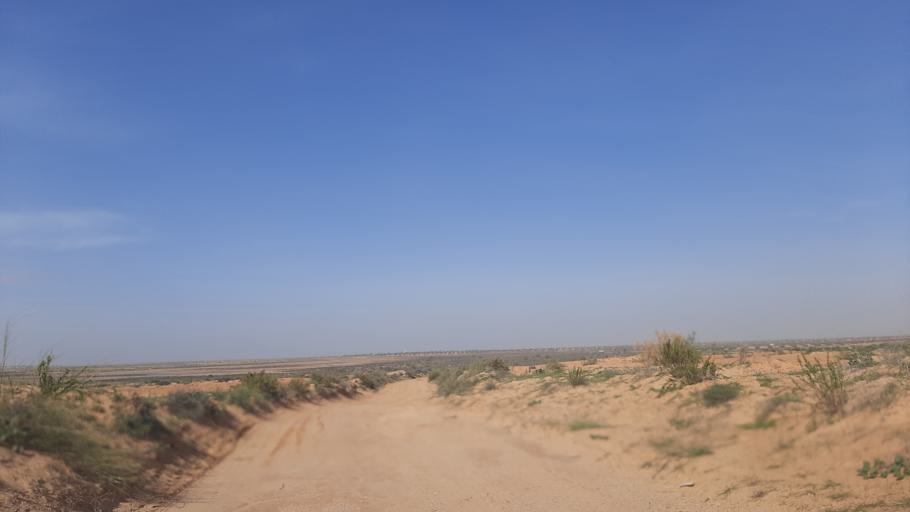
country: TN
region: Madanin
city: Zarzis
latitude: 33.4380
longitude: 10.8072
